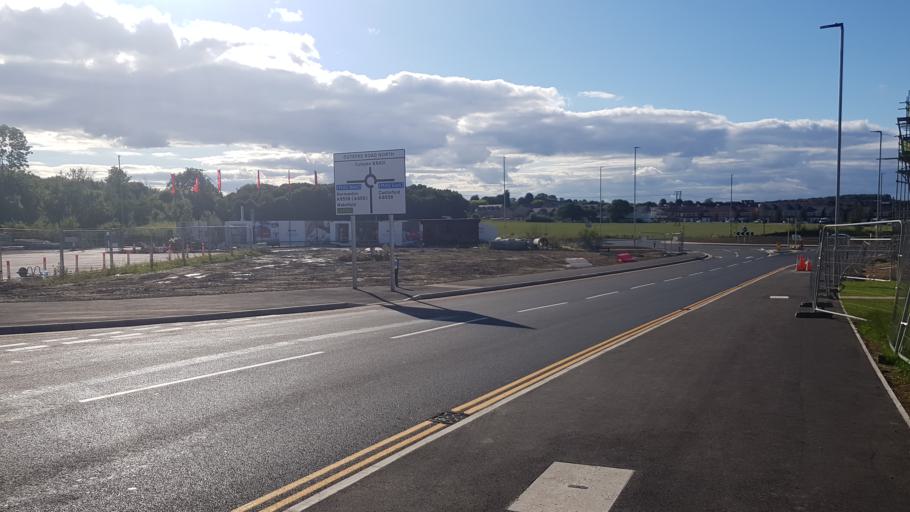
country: GB
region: England
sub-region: City and Borough of Wakefield
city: Castleford
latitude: 53.7077
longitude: -1.3661
